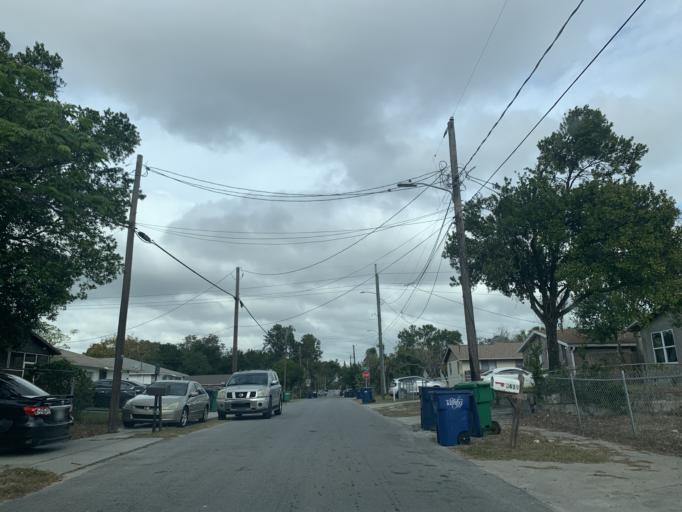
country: US
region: Florida
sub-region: Hillsborough County
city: East Lake-Orient Park
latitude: 27.9771
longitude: -82.3944
